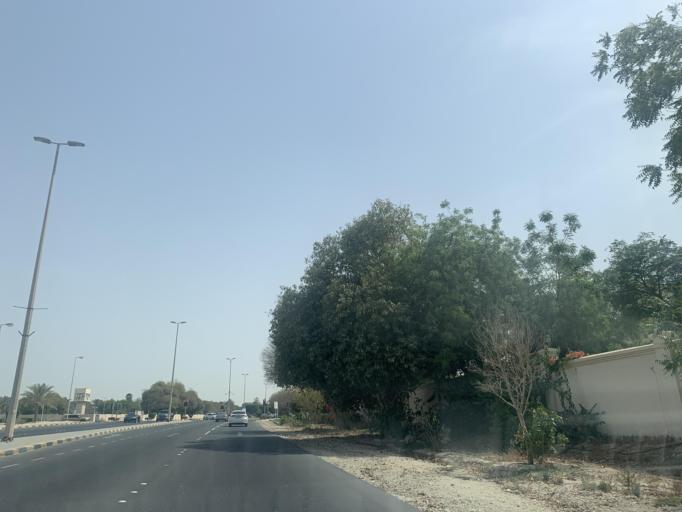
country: BH
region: Northern
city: Ar Rifa'
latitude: 26.1466
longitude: 50.5428
